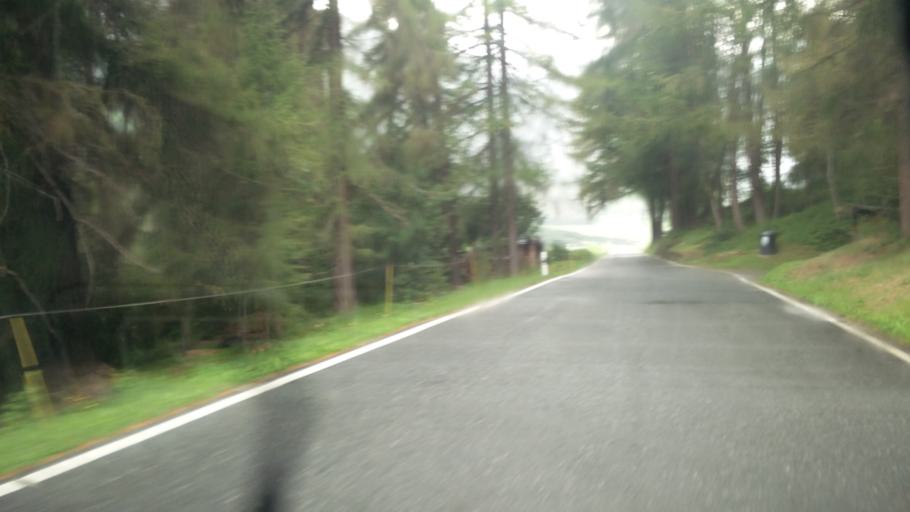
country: IT
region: Trentino-Alto Adige
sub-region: Bolzano
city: Tubre
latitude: 46.5982
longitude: 10.4303
